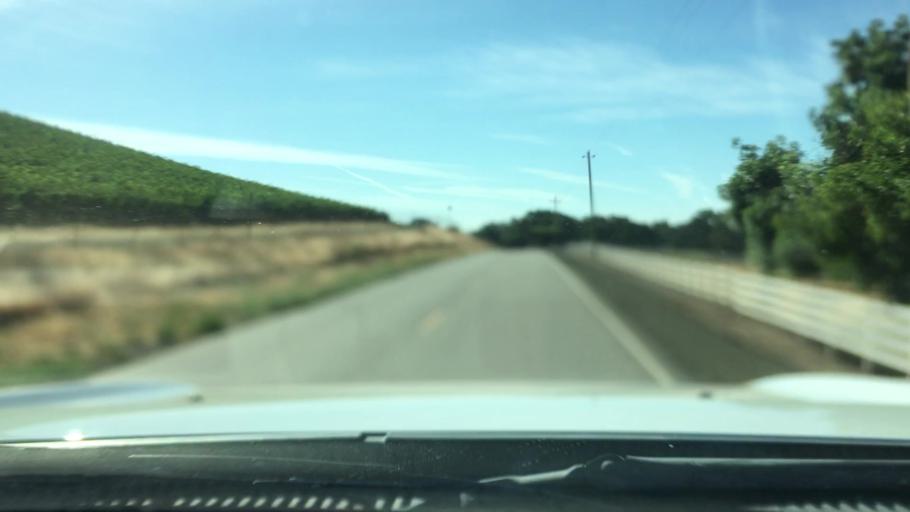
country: US
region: California
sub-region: San Luis Obispo County
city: Templeton
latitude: 35.5575
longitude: -120.6291
